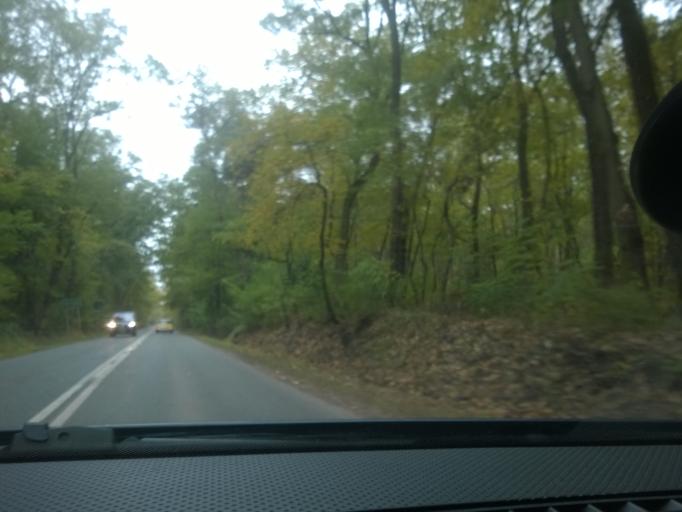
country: PL
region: Masovian Voivodeship
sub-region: Powiat pruszkowski
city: Granica
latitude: 52.1298
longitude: 20.8000
